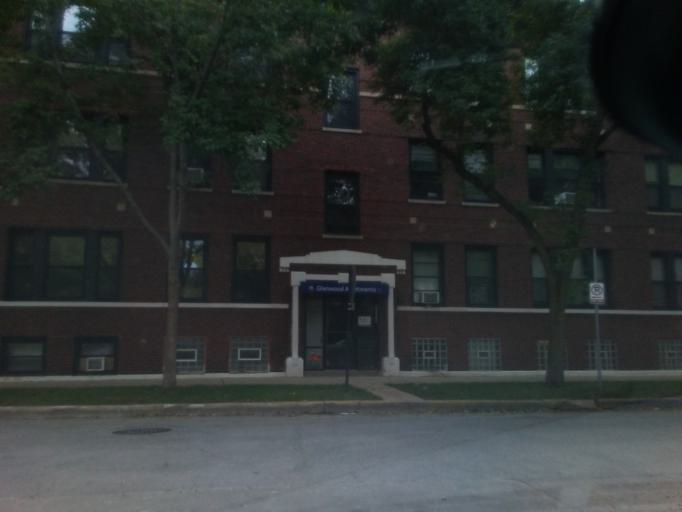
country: US
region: Illinois
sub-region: Cook County
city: Lincolnwood
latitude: 41.9734
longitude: -87.6648
